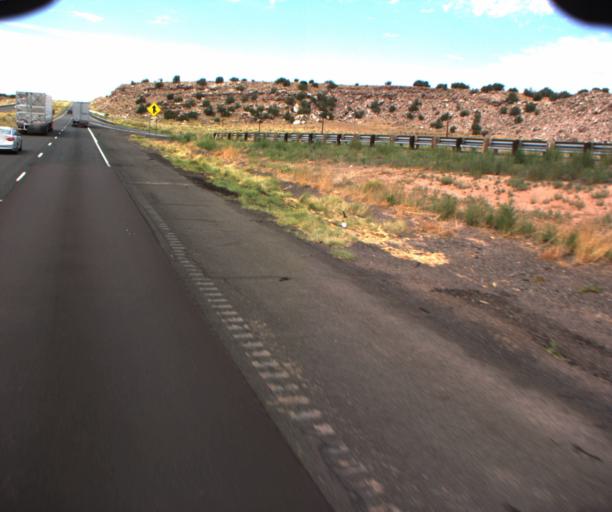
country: US
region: Arizona
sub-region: Apache County
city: Houck
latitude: 35.1639
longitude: -109.4873
